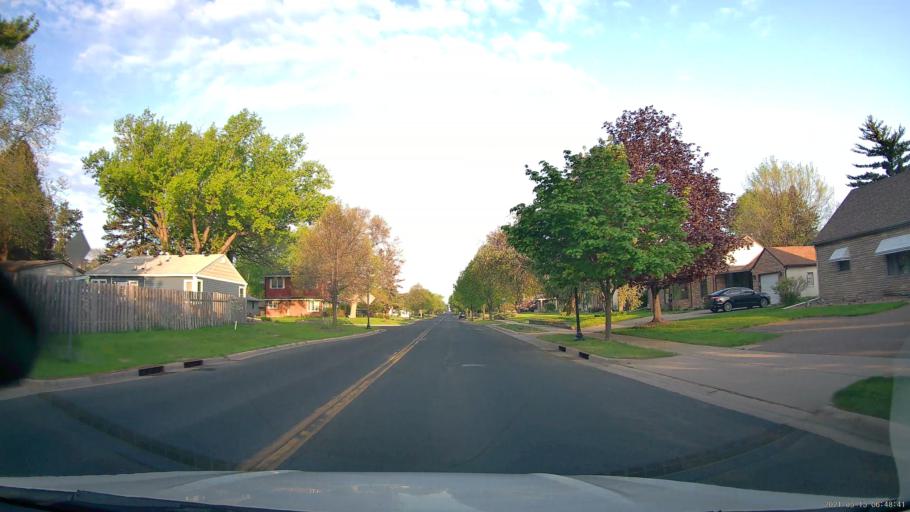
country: US
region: Minnesota
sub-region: Hennepin County
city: Saint Anthony
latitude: 45.0206
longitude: -93.2187
